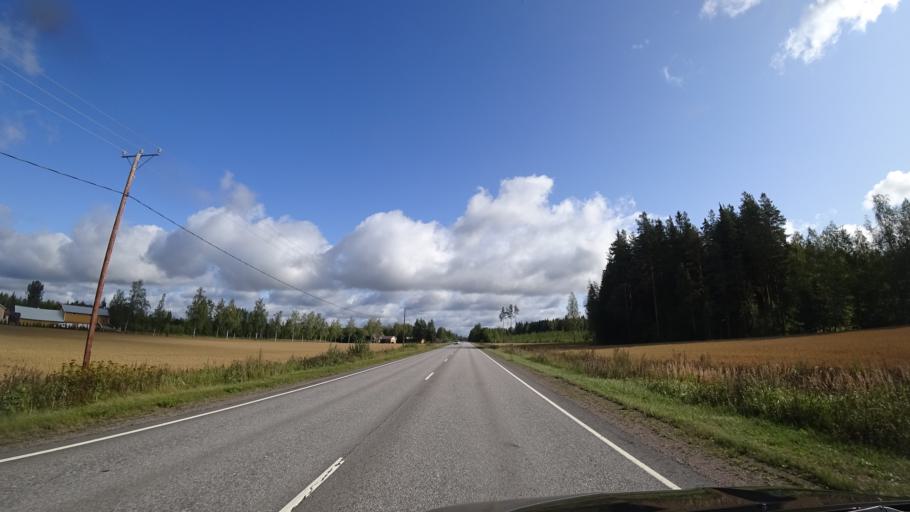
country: FI
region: Uusimaa
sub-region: Helsinki
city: Hyvinge
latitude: 60.5409
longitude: 24.9291
